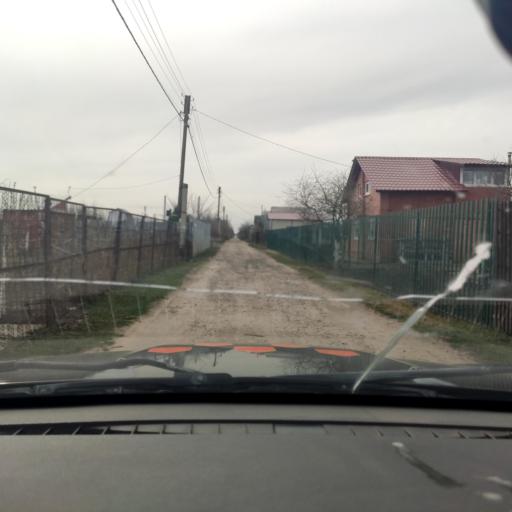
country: RU
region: Samara
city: Tol'yatti
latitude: 53.6040
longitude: 49.2477
